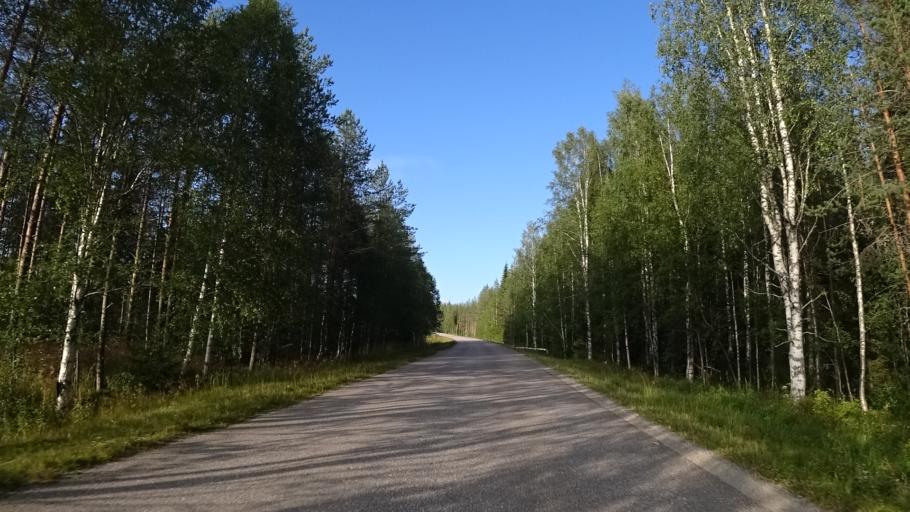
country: FI
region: North Karelia
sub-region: Joensuu
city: Eno
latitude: 63.0313
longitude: 30.5279
